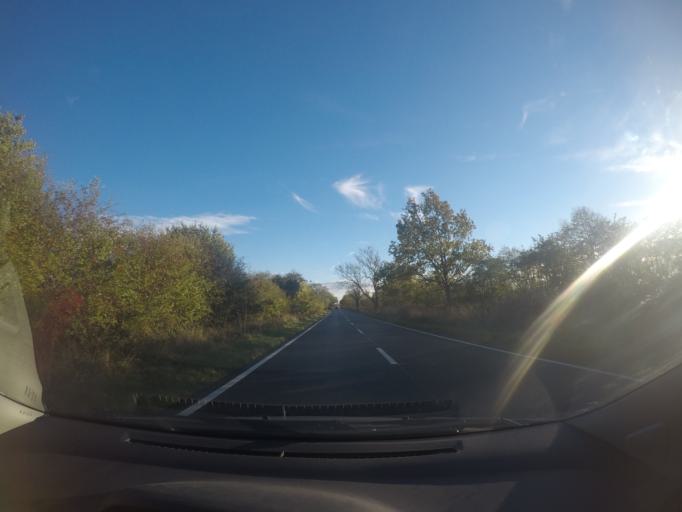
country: GB
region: England
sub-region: City of York
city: York
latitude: 53.9846
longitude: -1.0839
